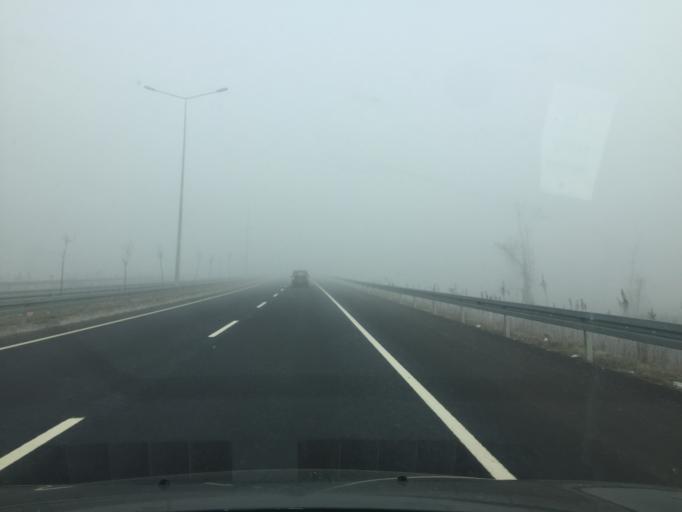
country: TR
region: Duzce
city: Duzce
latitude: 40.8142
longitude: 31.1691
